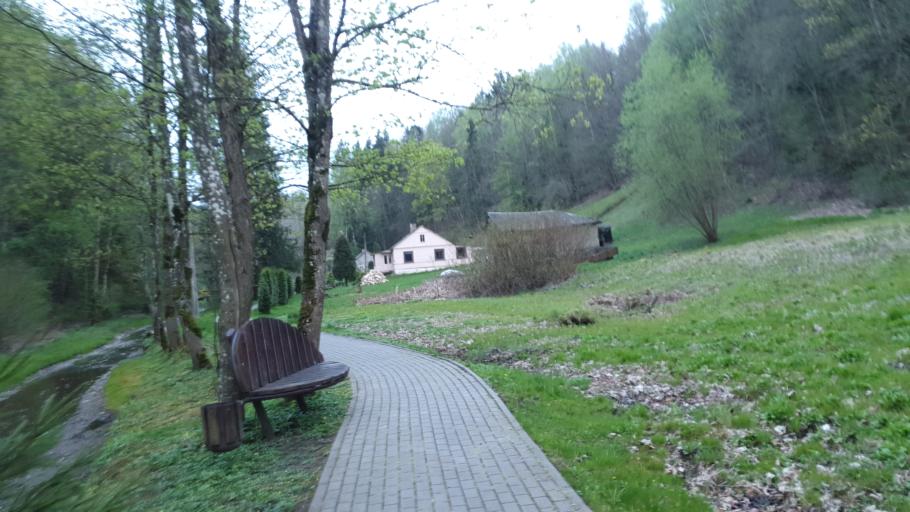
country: LT
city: Sakiai
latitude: 55.0812
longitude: 23.1781
